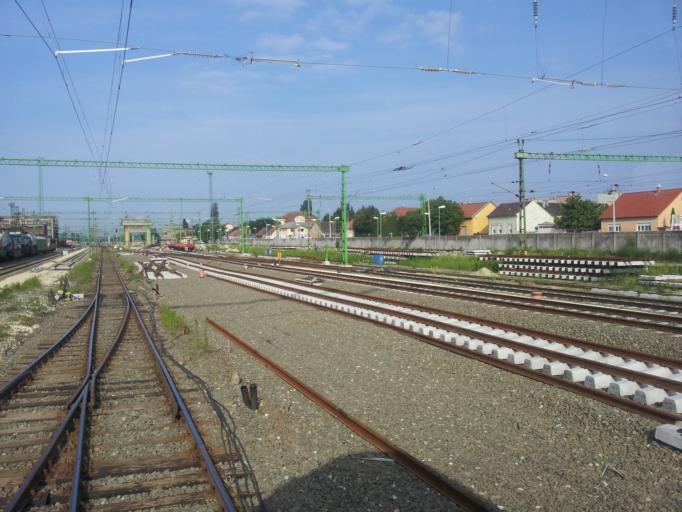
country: HU
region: Fejer
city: Szekesfehervar
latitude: 47.1851
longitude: 18.4317
